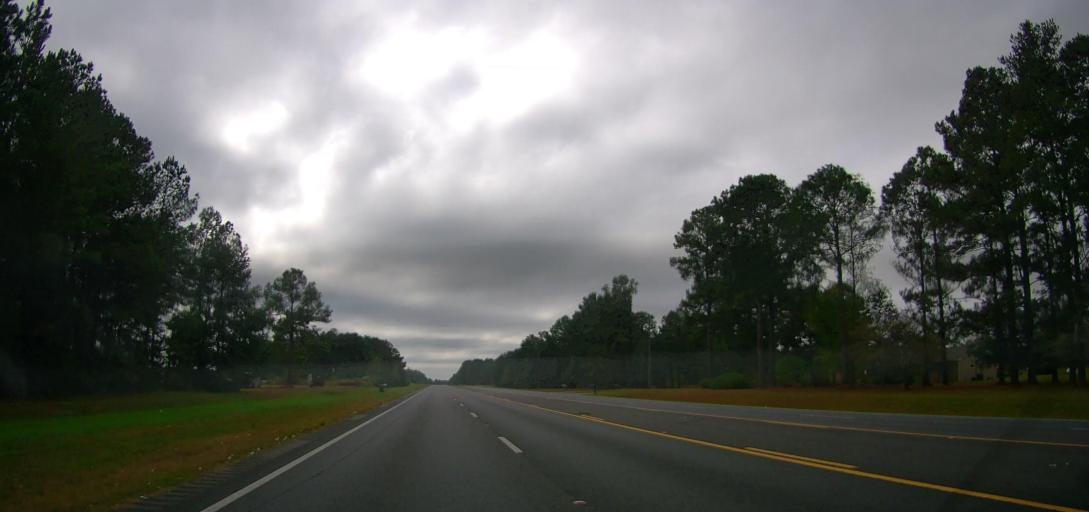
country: US
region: Georgia
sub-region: Colquitt County
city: Moultrie
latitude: 31.0595
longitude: -83.8307
